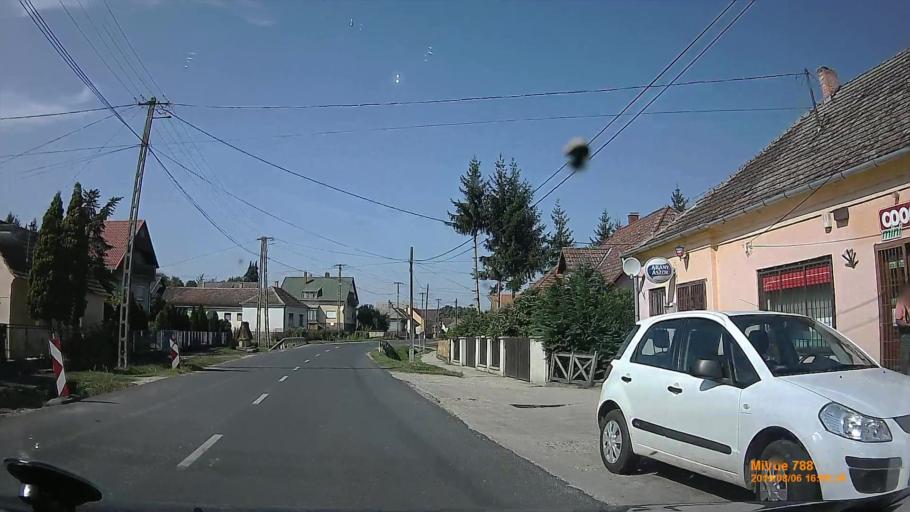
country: HU
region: Zala
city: Murakeresztur
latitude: 46.3209
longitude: 16.9696
